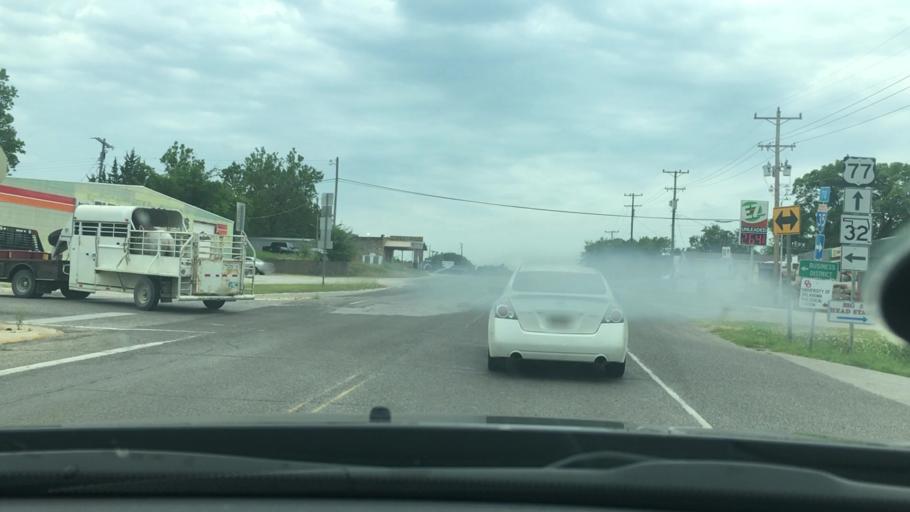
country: US
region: Oklahoma
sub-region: Love County
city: Marietta
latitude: 33.9380
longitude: -97.1263
